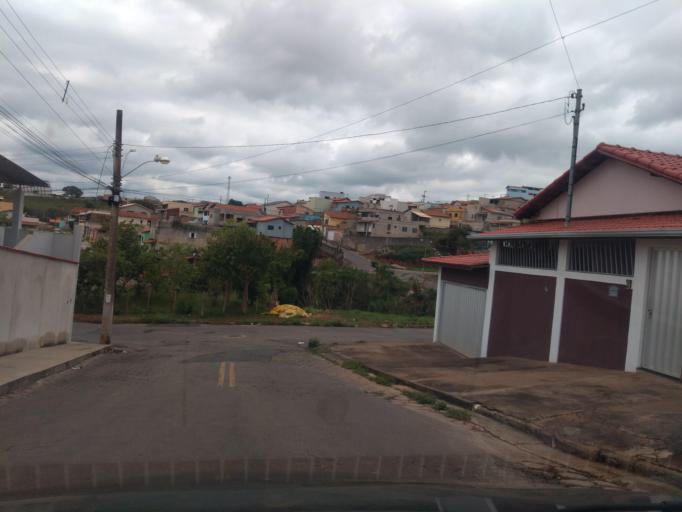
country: BR
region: Minas Gerais
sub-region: Tres Coracoes
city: Tres Coracoes
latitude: -21.6888
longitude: -45.2507
